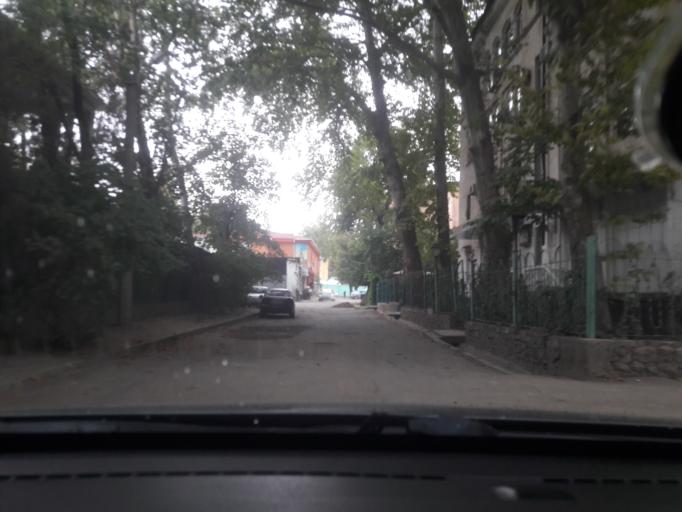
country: TJ
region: Dushanbe
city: Dushanbe
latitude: 38.5635
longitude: 68.7910
